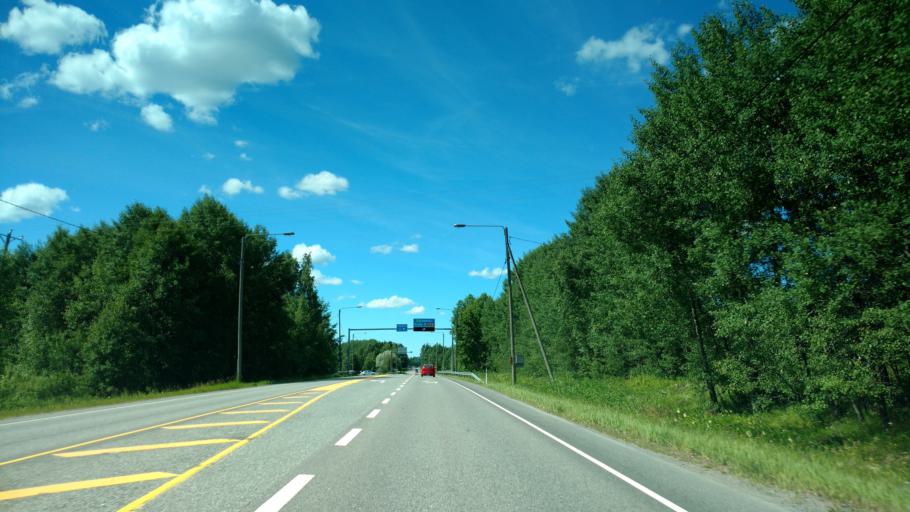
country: FI
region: Varsinais-Suomi
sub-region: Turku
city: Piikkioe
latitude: 60.4496
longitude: 22.4624
